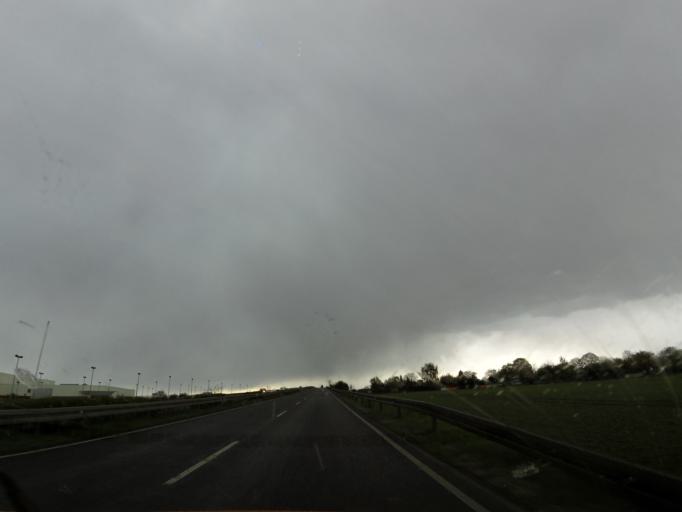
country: DE
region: Saxony-Anhalt
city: Hohendodeleben
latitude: 52.0405
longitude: 11.5187
